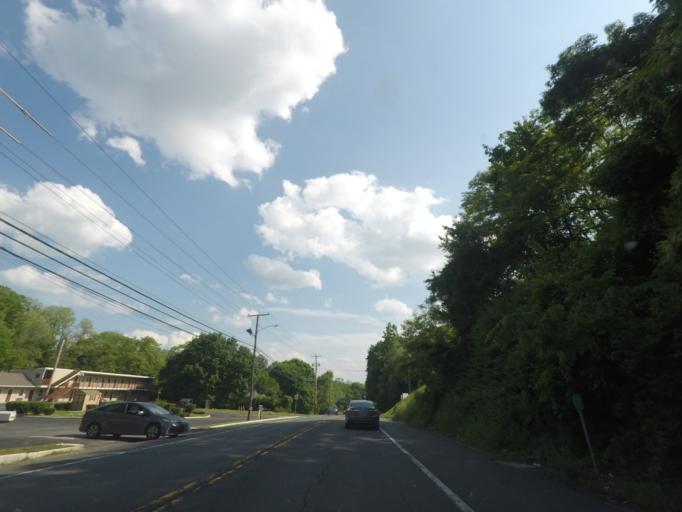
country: US
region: New York
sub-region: Orange County
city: Balmville
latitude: 41.5400
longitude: -74.0129
